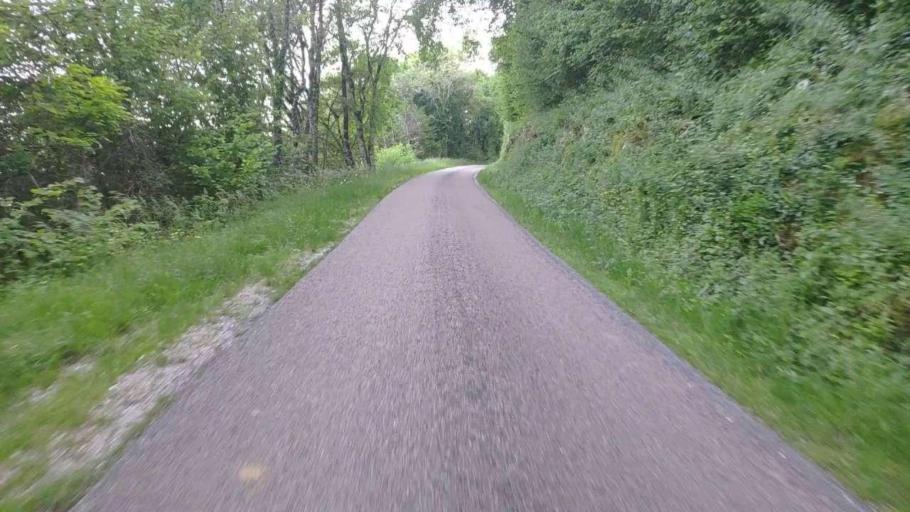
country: FR
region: Franche-Comte
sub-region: Departement du Jura
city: Perrigny
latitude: 46.7191
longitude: 5.6052
